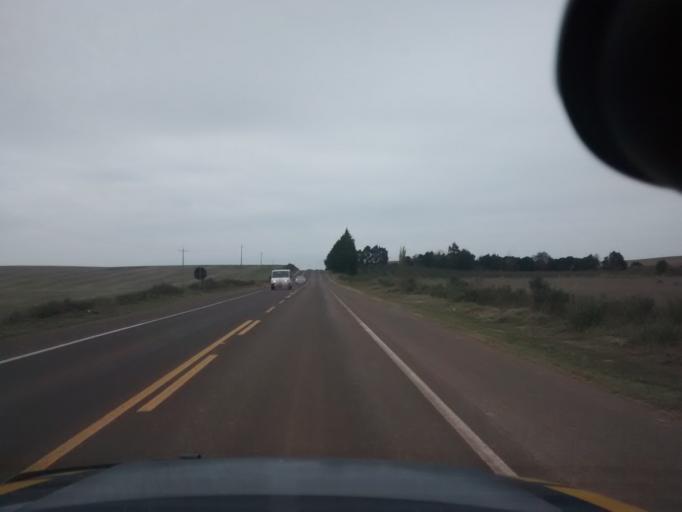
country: BR
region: Rio Grande do Sul
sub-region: Vacaria
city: Vacaria
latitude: -28.4524
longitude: -50.9895
